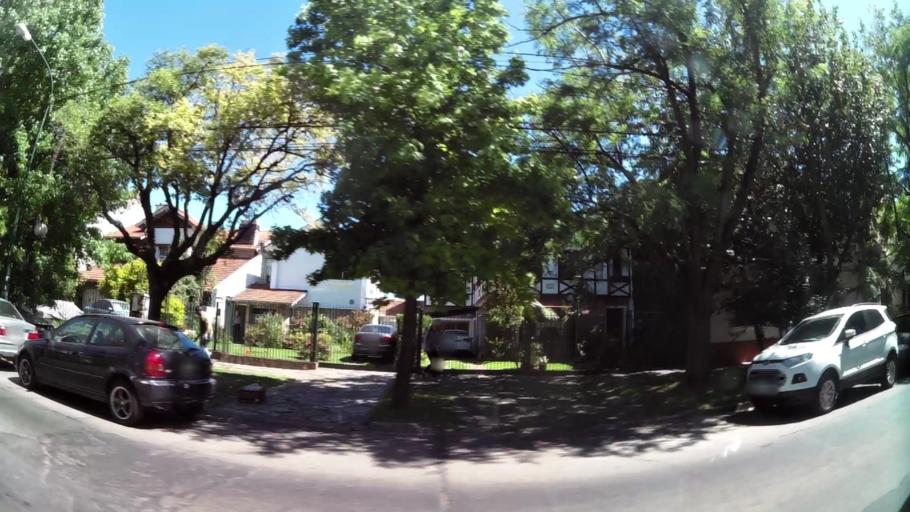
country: AR
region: Buenos Aires
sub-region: Partido de Vicente Lopez
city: Olivos
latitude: -34.4973
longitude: -58.4966
